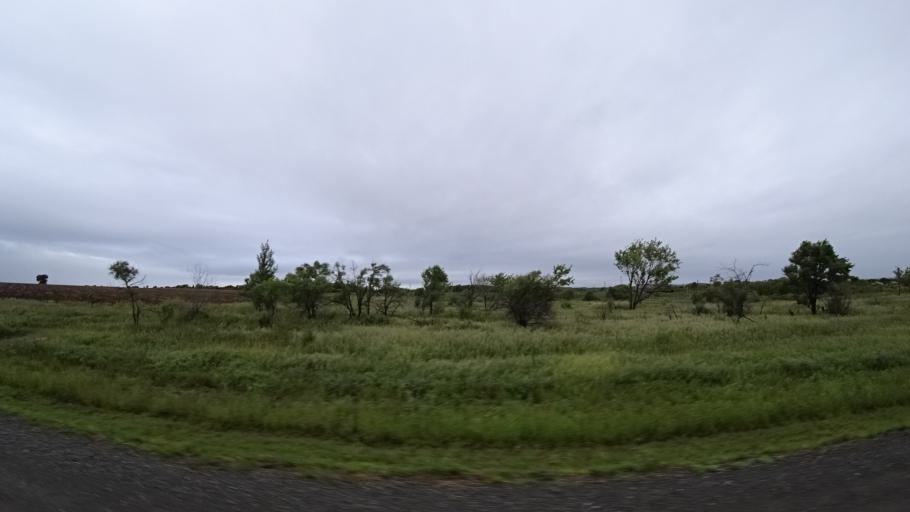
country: RU
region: Primorskiy
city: Chernigovka
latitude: 44.3220
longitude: 132.5690
